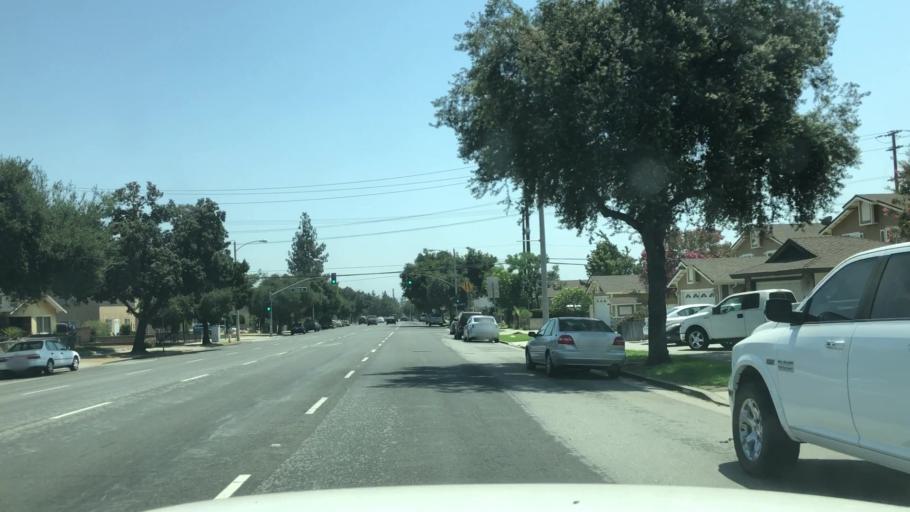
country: US
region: California
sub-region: Los Angeles County
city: Azusa
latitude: 34.1270
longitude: -117.9089
